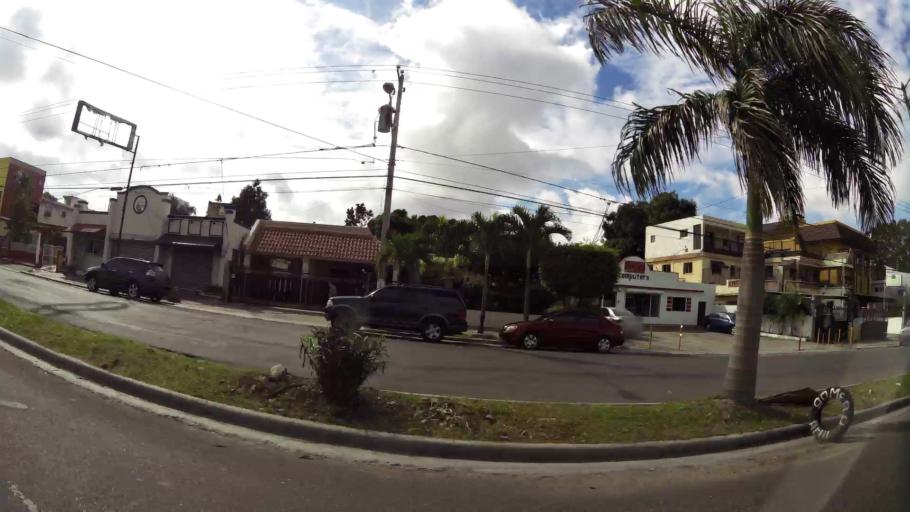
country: DO
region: Santiago
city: Santiago de los Caballeros
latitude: 19.4613
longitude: -70.6799
